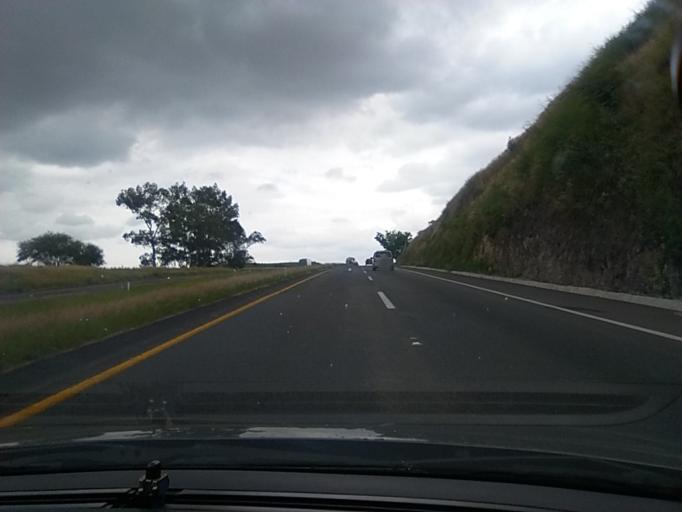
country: MX
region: Jalisco
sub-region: Poncitlan
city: Santa Cruz el Grande
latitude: 20.4411
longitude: -102.8199
